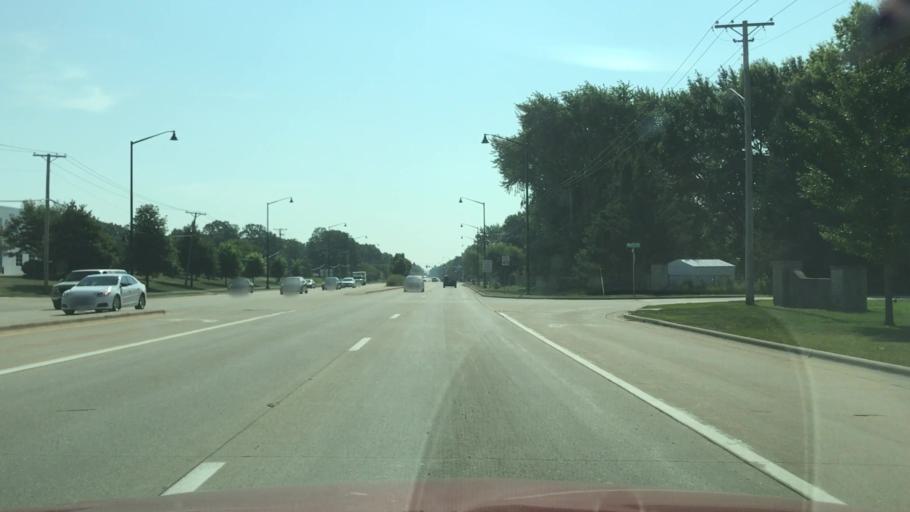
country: US
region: Illinois
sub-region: Winnebago County
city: Cherry Valley
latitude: 42.2384
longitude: -89.0039
